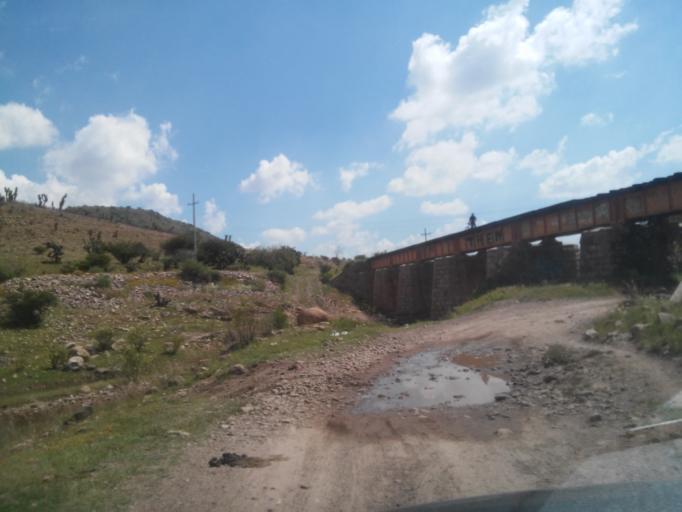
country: MX
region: Durango
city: Victoria de Durango
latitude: 24.0133
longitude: -104.7426
